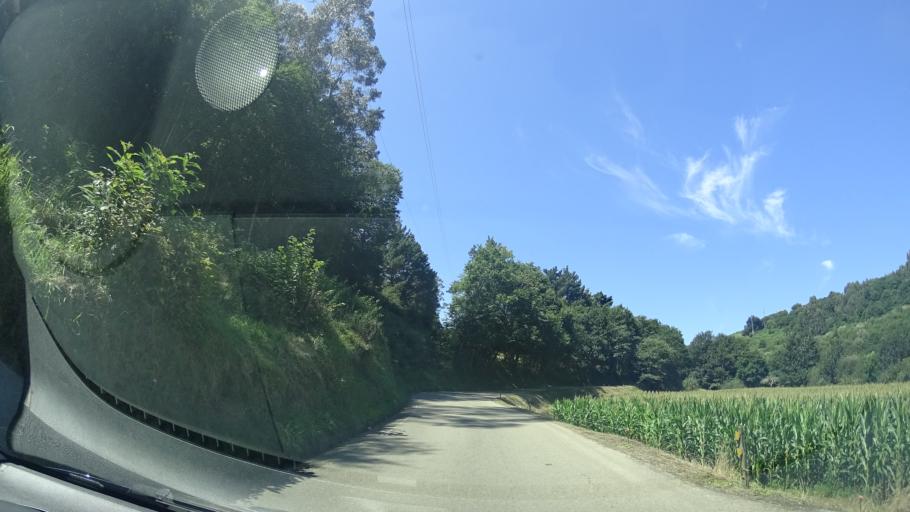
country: ES
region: Asturias
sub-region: Province of Asturias
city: Ribadesella
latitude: 43.4385
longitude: -5.0793
